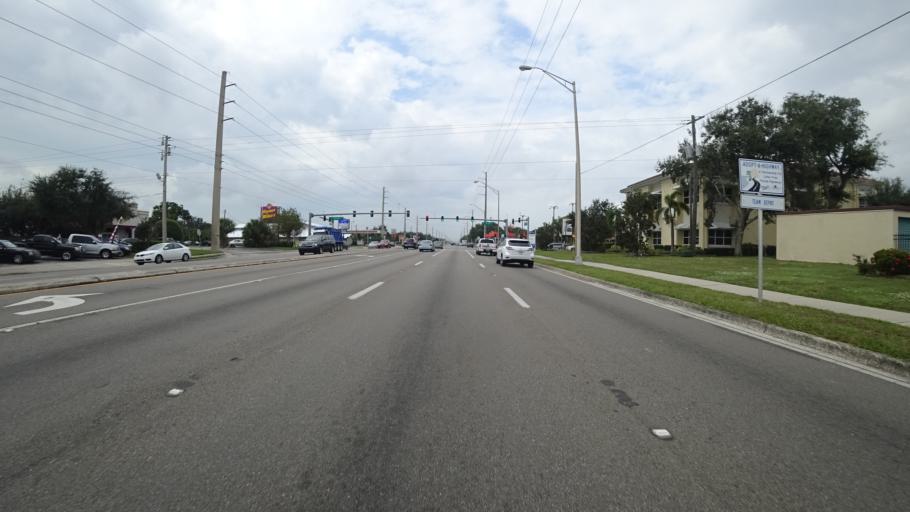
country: US
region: Florida
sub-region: Manatee County
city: South Bradenton
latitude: 27.4626
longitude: -82.5805
